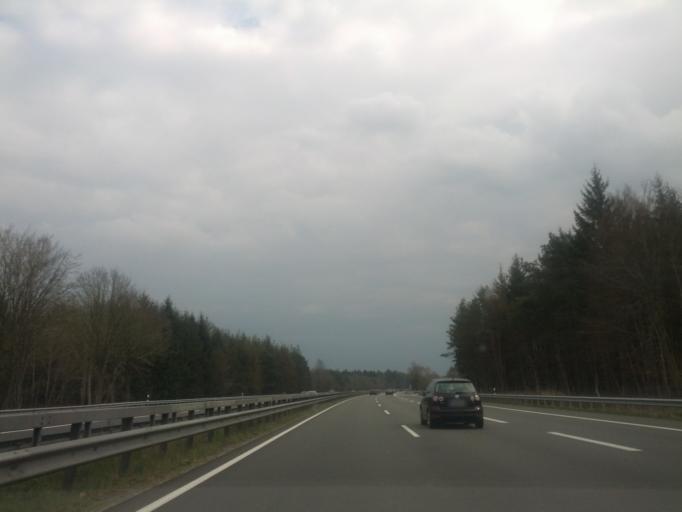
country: DE
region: Lower Saxony
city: Bad Zwischenahn
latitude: 53.2494
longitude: 8.0006
